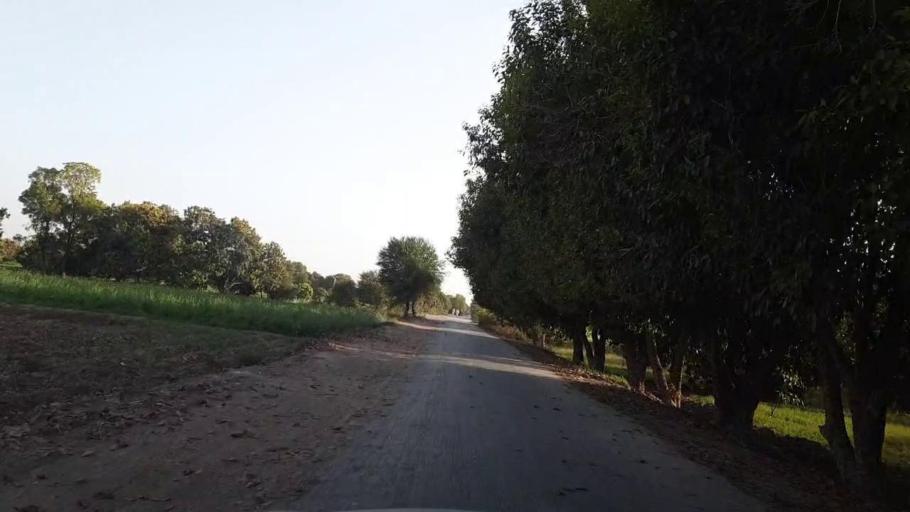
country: PK
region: Sindh
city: Tando Ghulam Ali
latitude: 25.1262
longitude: 68.9069
